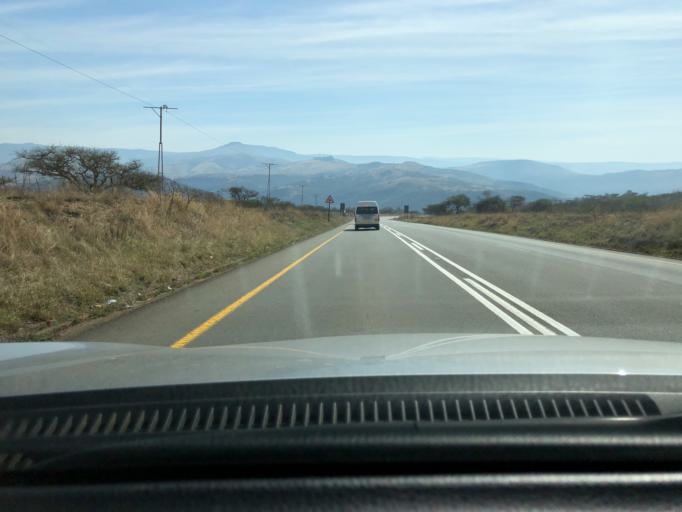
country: ZA
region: KwaZulu-Natal
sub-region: uMgungundlovu District Municipality
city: Richmond
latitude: -30.0280
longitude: 30.2210
